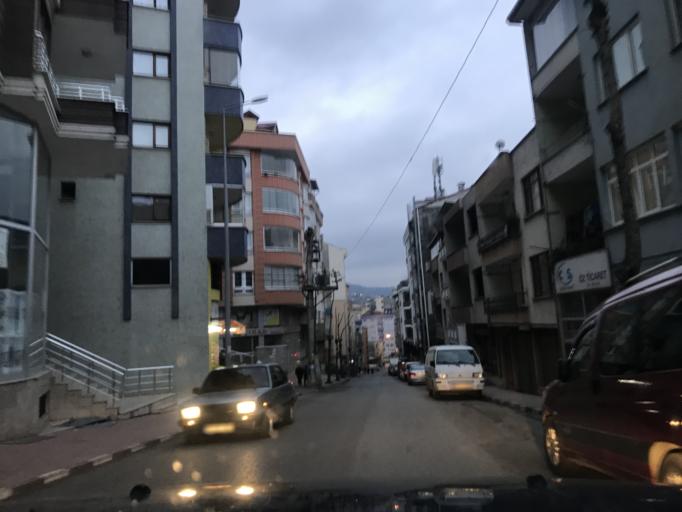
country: TR
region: Trabzon
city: Akcaabat
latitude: 41.0186
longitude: 39.5814
